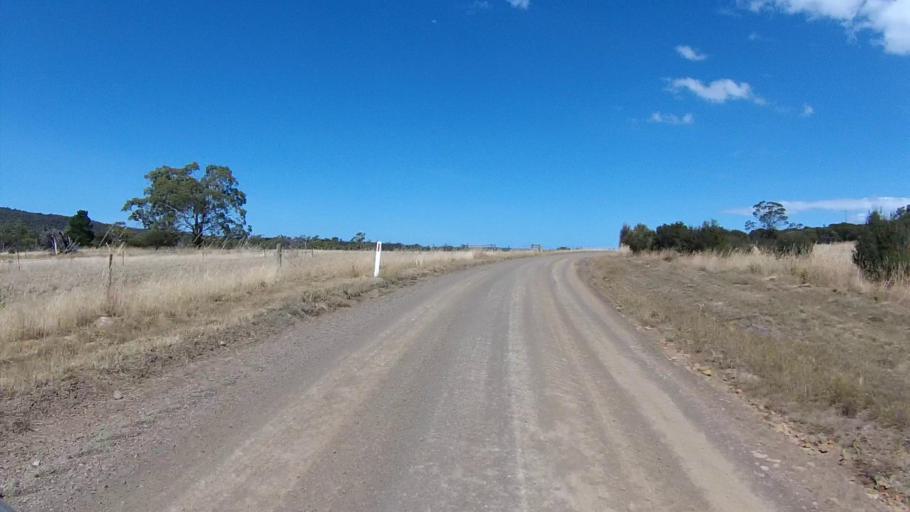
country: AU
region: Tasmania
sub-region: Break O'Day
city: St Helens
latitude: -41.9673
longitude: 148.0743
